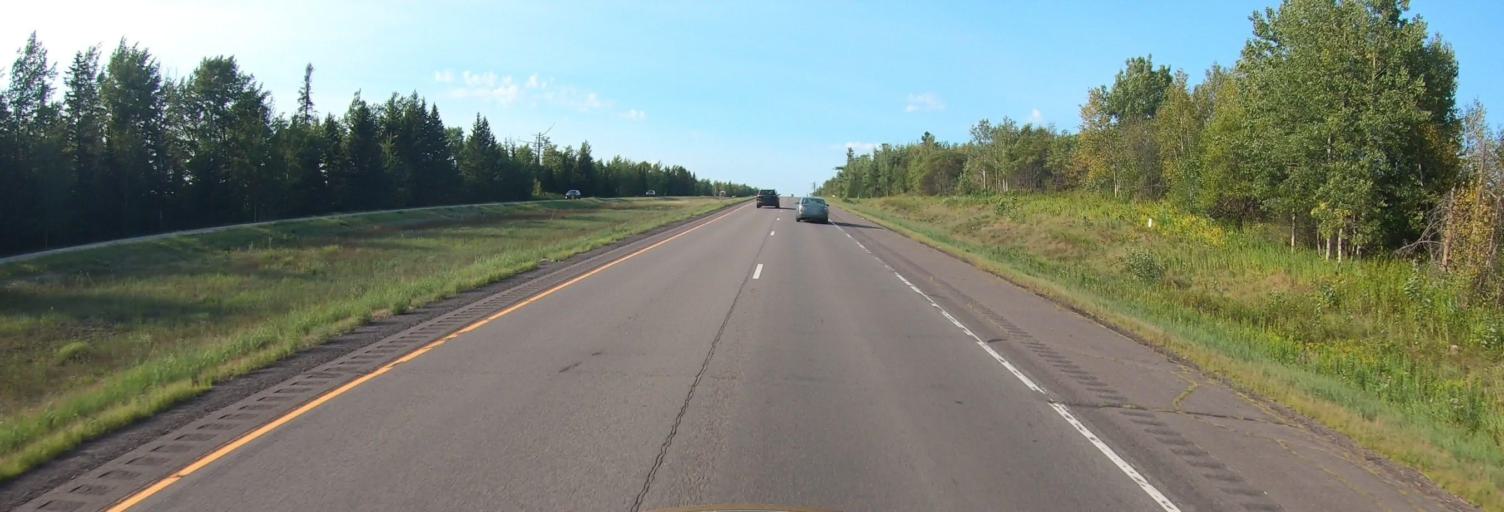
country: US
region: Minnesota
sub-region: Carlton County
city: Cloquet
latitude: 47.0050
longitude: -92.4710
